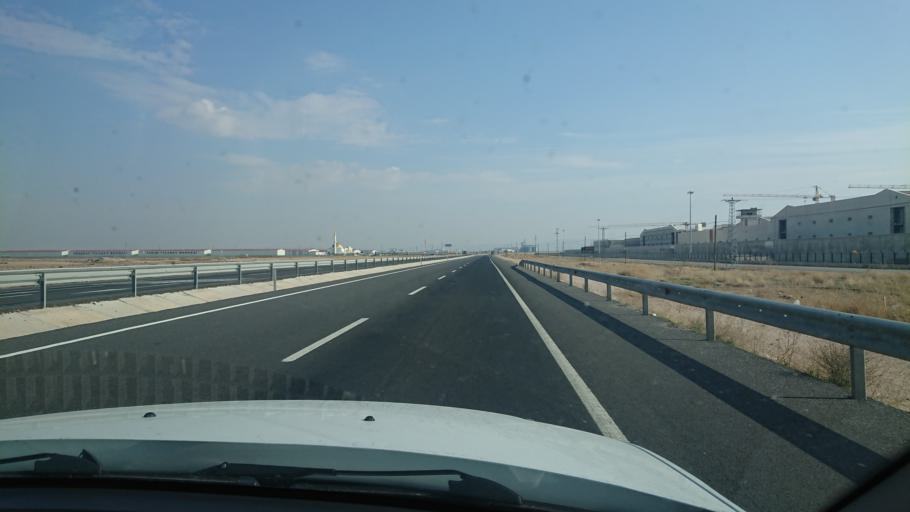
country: TR
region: Aksaray
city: Aksaray
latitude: 38.3352
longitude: 33.9234
